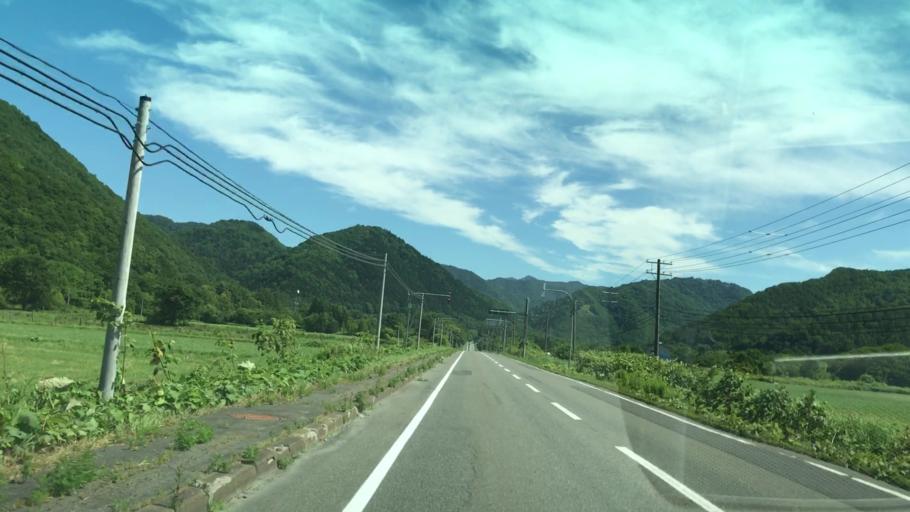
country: JP
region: Hokkaido
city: Shimo-furano
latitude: 42.8854
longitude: 142.4588
